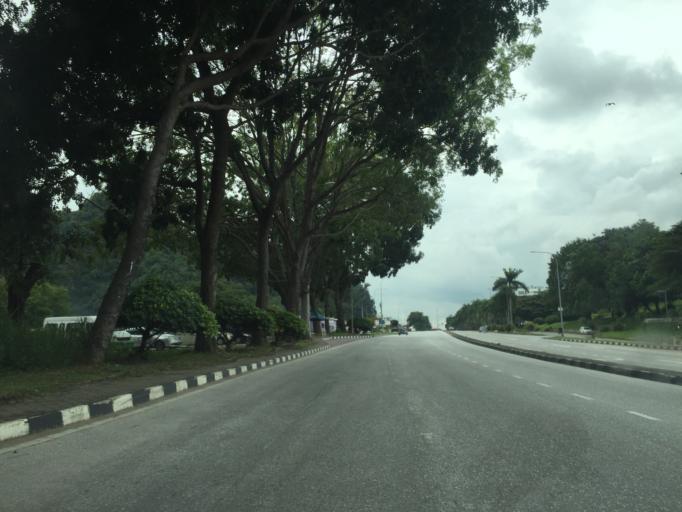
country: MY
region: Perak
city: Ipoh
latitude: 4.5666
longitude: 101.1136
